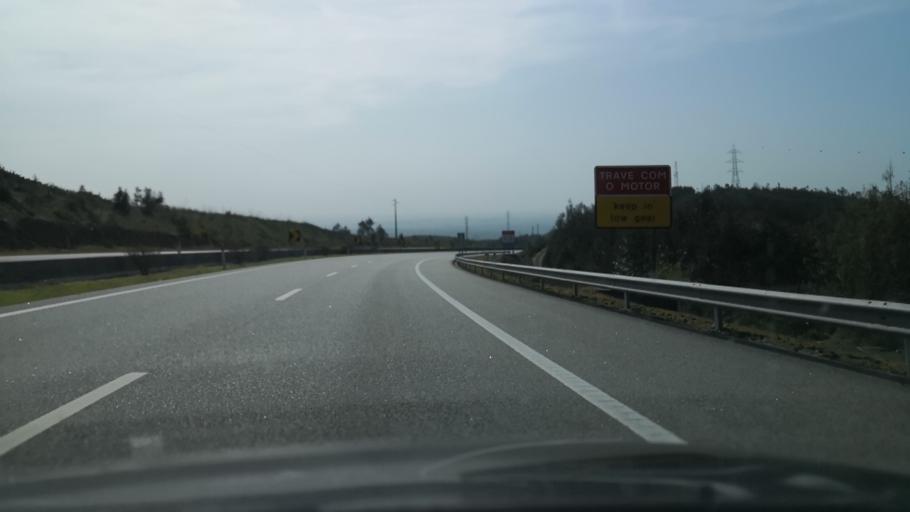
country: PT
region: Aveiro
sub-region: Sever do Vouga
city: Sever do Vouga
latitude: 40.6557
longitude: -8.3623
